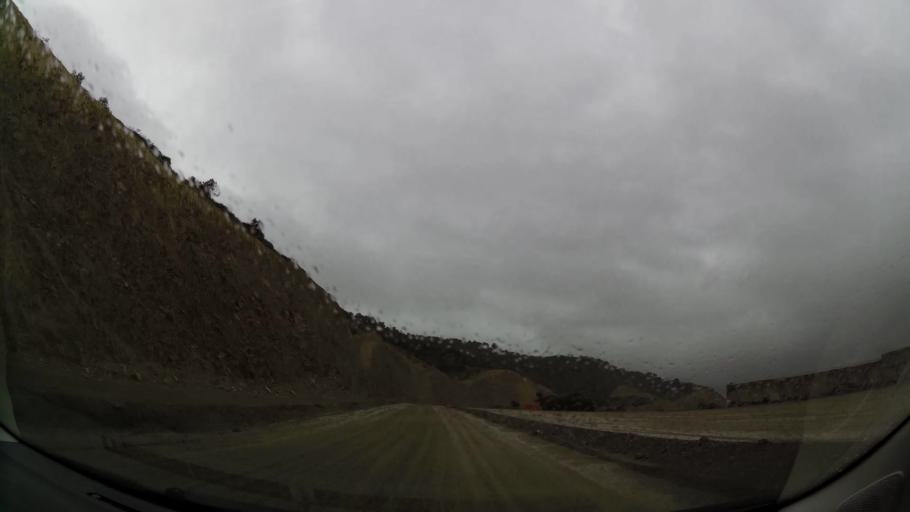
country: MA
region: Taza-Al Hoceima-Taounate
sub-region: Taza
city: Ajdir
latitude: 34.8982
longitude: -3.7824
